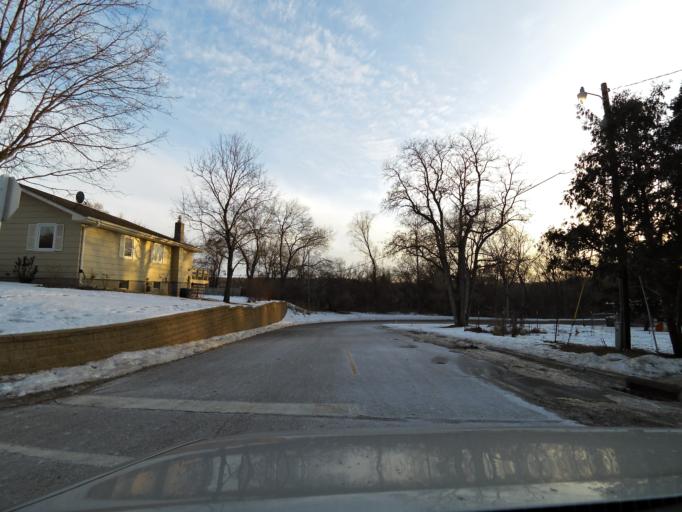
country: US
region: Wisconsin
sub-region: Saint Croix County
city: North Hudson
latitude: 44.9927
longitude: -92.7518
